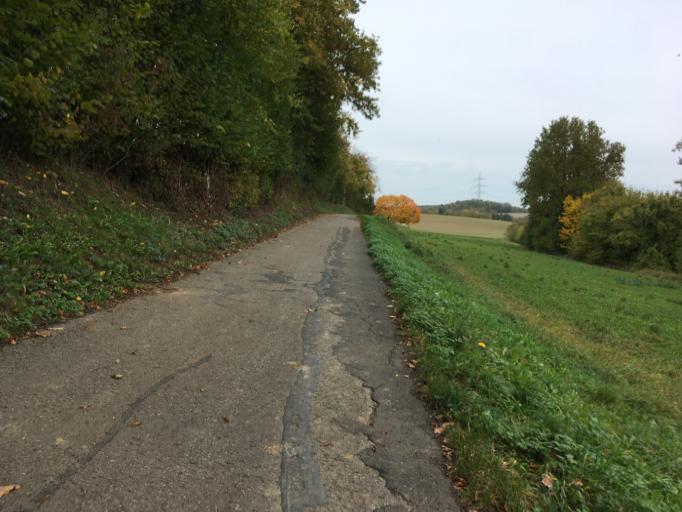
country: DE
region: Baden-Wuerttemberg
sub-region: Karlsruhe Region
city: Seckach
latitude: 49.4540
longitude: 9.3289
